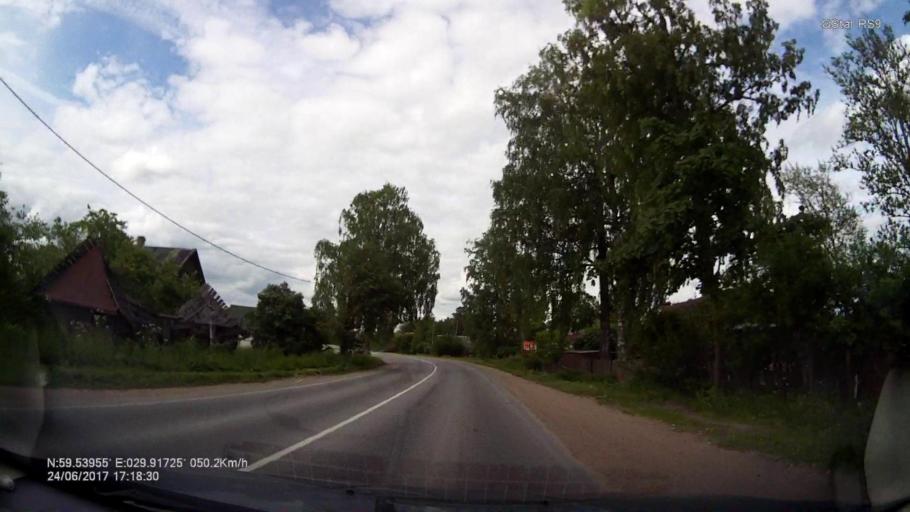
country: RU
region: Leningrad
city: Voyskovitsy
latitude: 59.5396
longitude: 29.9174
